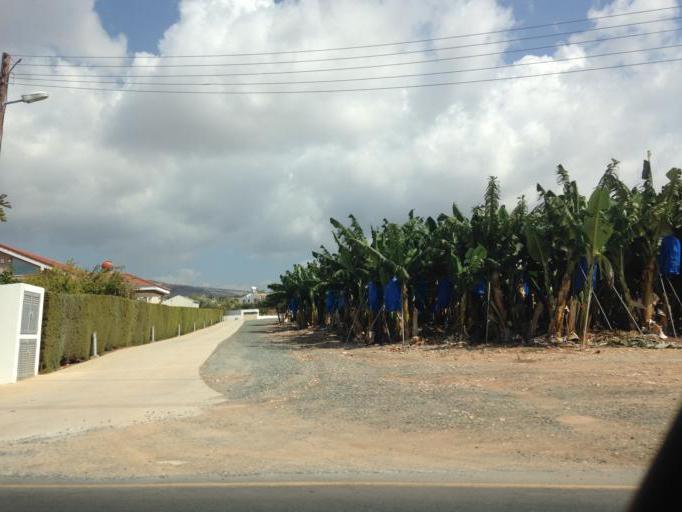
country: CY
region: Pafos
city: Pegeia
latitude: 34.8612
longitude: 32.3797
